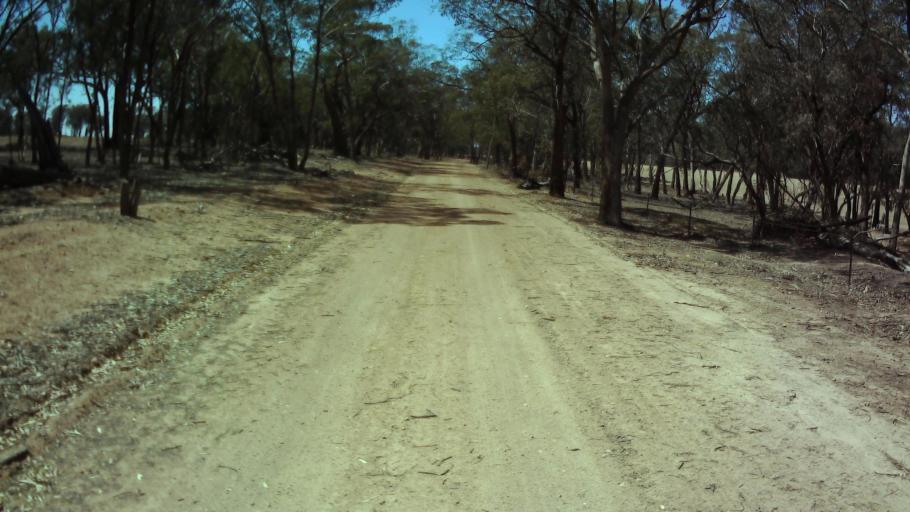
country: AU
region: New South Wales
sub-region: Weddin
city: Grenfell
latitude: -33.9624
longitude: 148.0885
